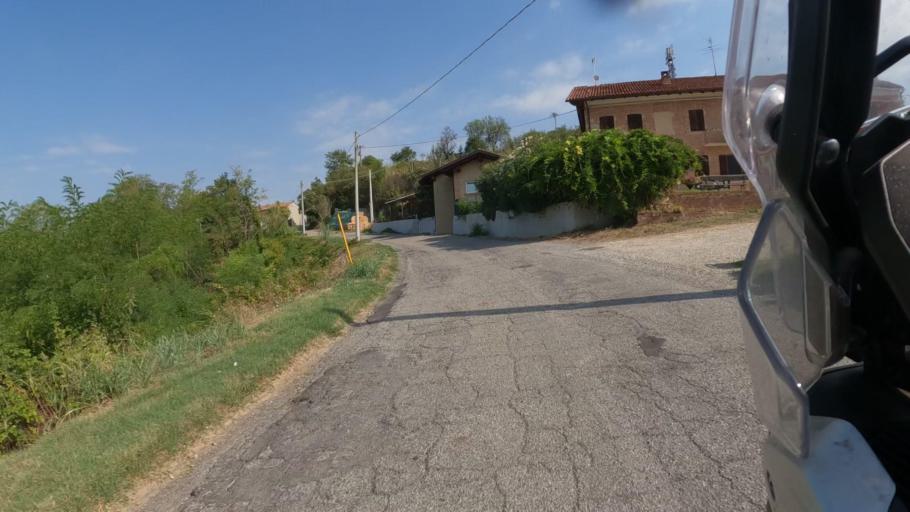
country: IT
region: Piedmont
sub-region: Provincia di Alessandria
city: Altavilla Monferrato
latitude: 44.9741
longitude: 8.3877
